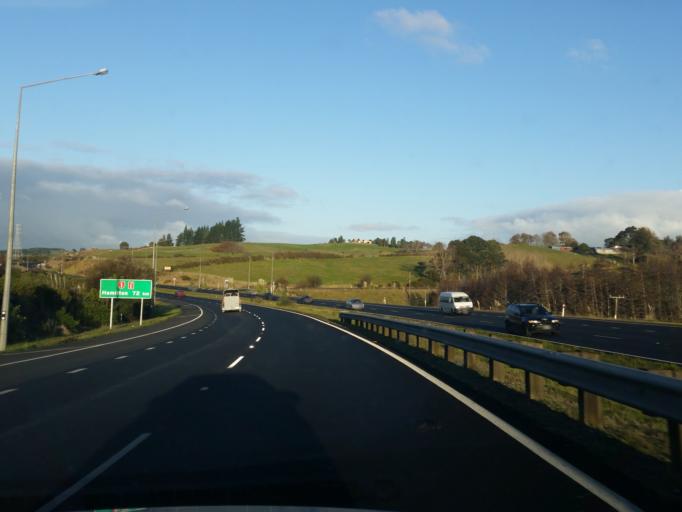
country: NZ
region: Auckland
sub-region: Auckland
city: Pukekohe East
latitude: -37.2517
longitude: 175.0301
